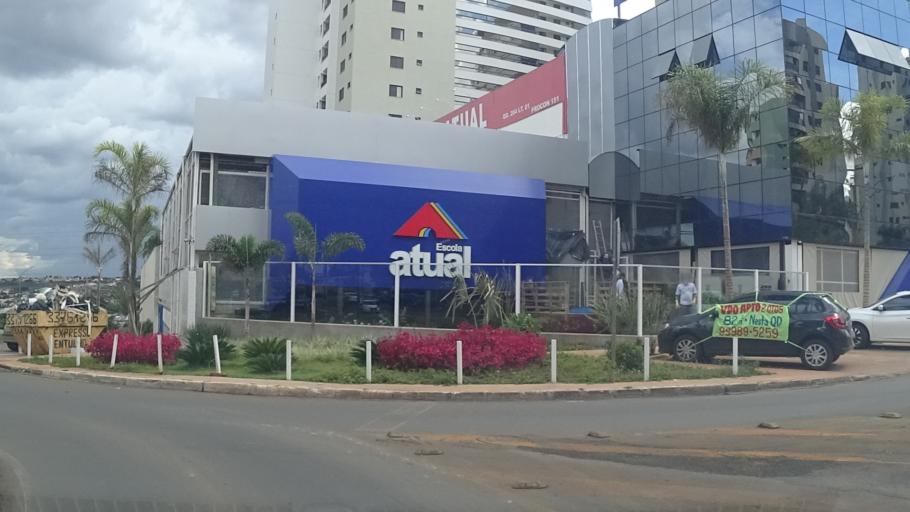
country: BR
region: Federal District
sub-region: Brasilia
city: Brasilia
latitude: -15.8406
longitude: -48.0180
